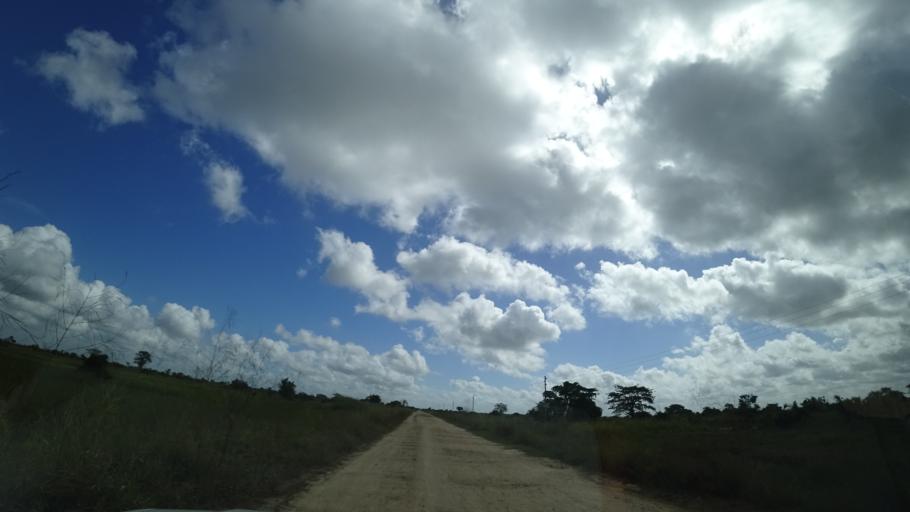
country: MZ
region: Sofala
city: Dondo
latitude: -19.4371
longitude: 34.5614
